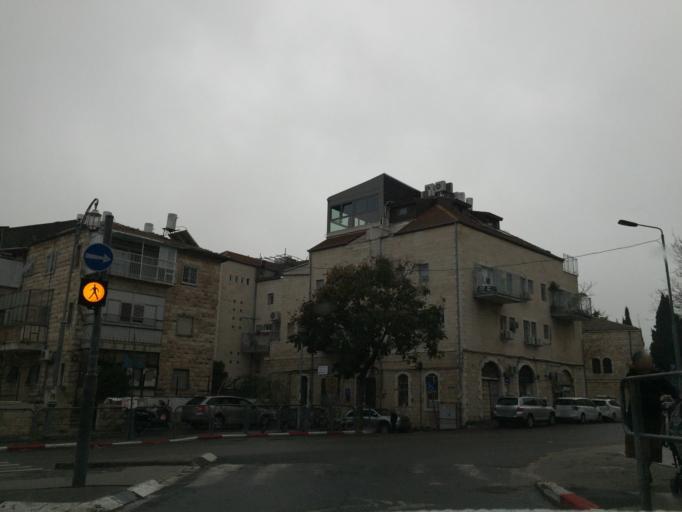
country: IL
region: Jerusalem
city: West Jerusalem
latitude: 31.7849
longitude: 35.2249
